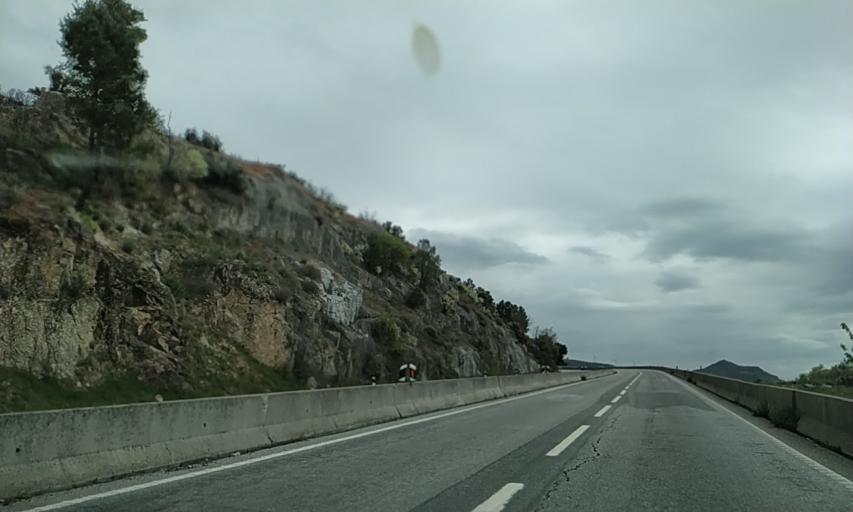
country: PT
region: Guarda
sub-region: Guarda
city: Guarda
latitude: 40.6063
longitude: -7.2829
